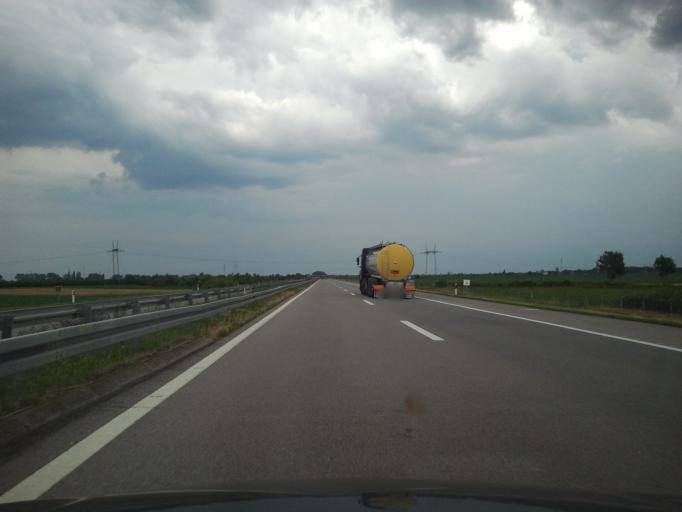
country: RS
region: Autonomna Pokrajina Vojvodina
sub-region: Sremski Okrug
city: Sremska Mitrovica
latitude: 45.0111
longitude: 19.5864
